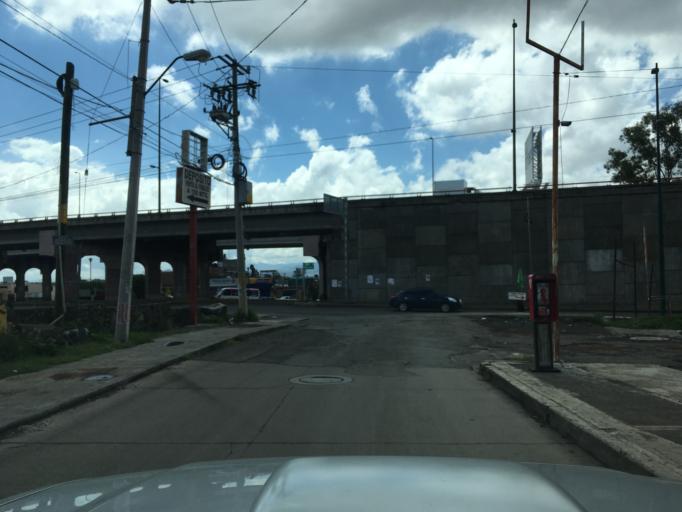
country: MX
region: Michoacan
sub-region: Tarimbaro
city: Fraccionamiento Metropolis II
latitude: 19.7248
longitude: -101.2251
